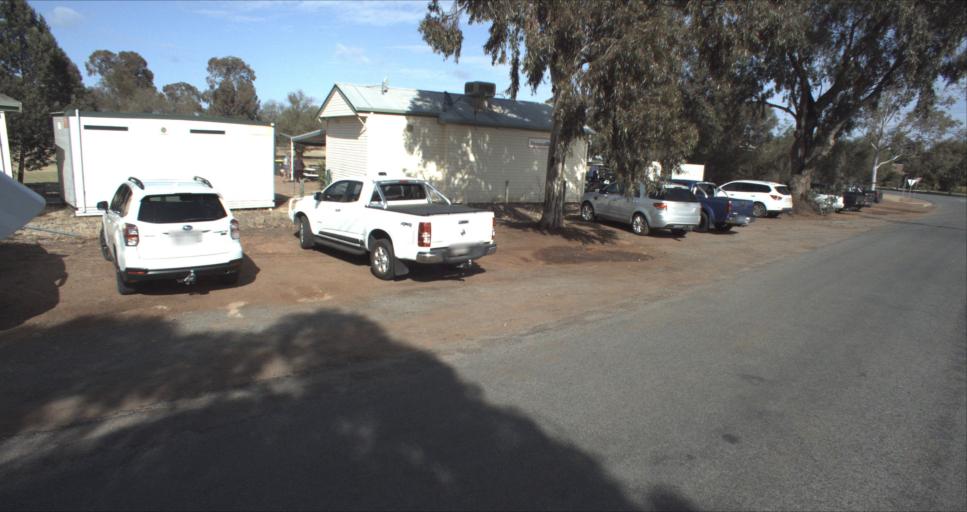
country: AU
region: New South Wales
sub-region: Leeton
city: Leeton
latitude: -34.5574
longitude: 146.4090
